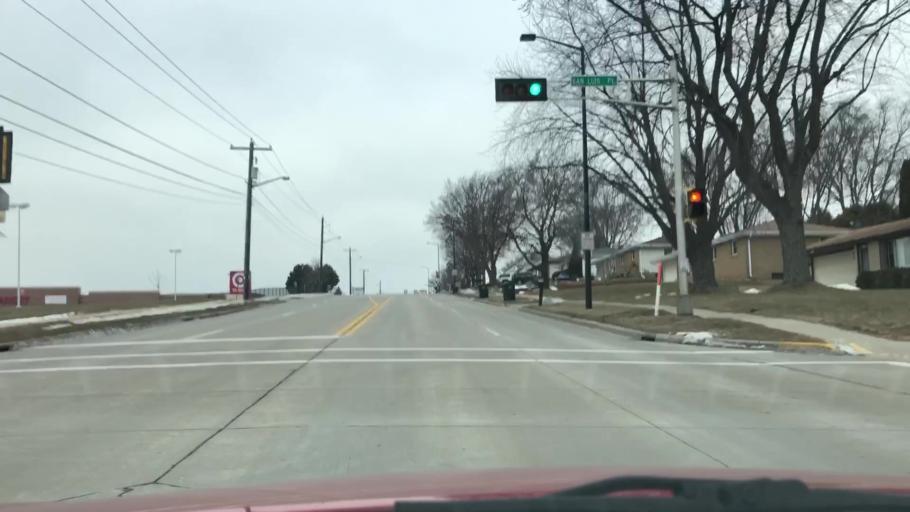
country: US
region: Wisconsin
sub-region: Brown County
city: Ashwaubenon
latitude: 44.4905
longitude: -88.0679
